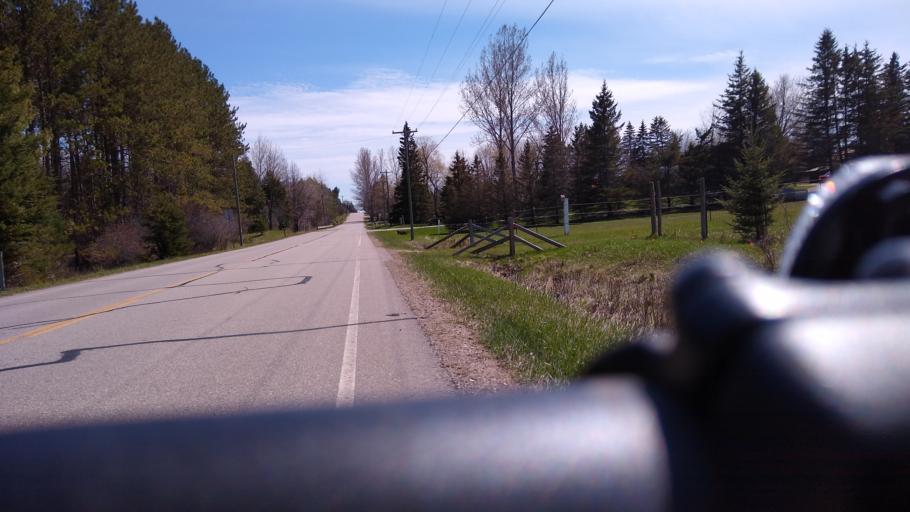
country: US
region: Michigan
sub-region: Delta County
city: Escanaba
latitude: 45.7261
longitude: -87.2025
